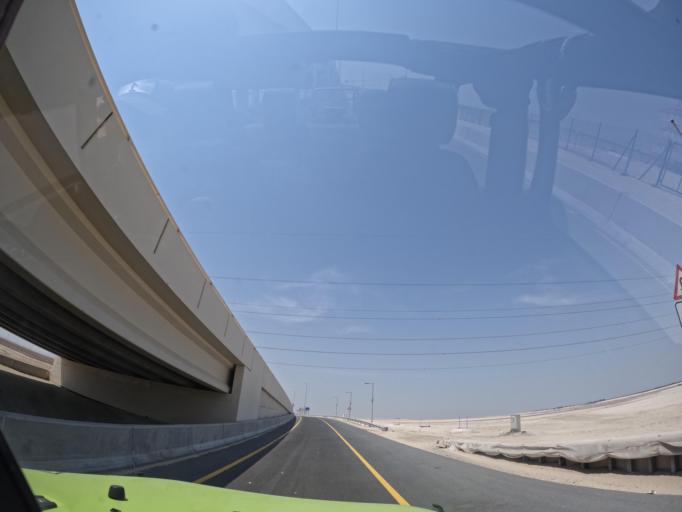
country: AE
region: Abu Dhabi
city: Abu Dhabi
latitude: 24.1647
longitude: 54.3536
